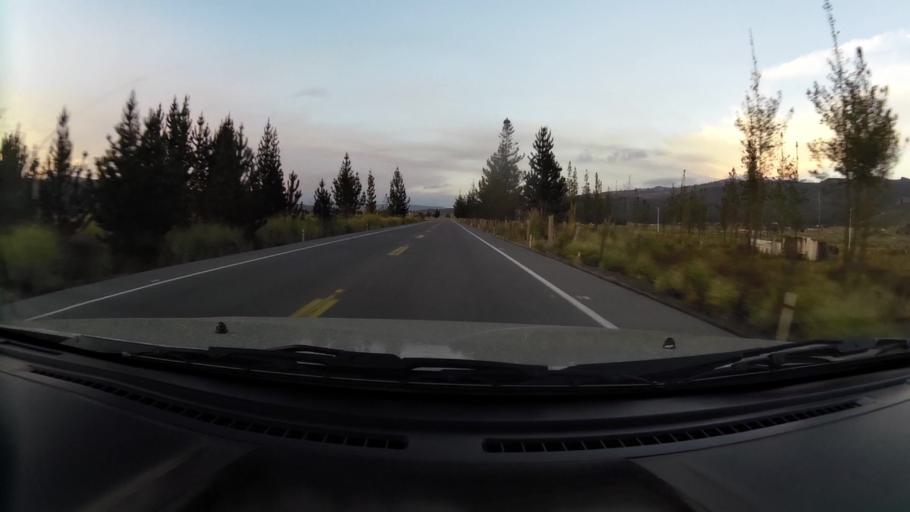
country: EC
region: Chimborazo
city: Alausi
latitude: -2.0208
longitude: -78.7317
